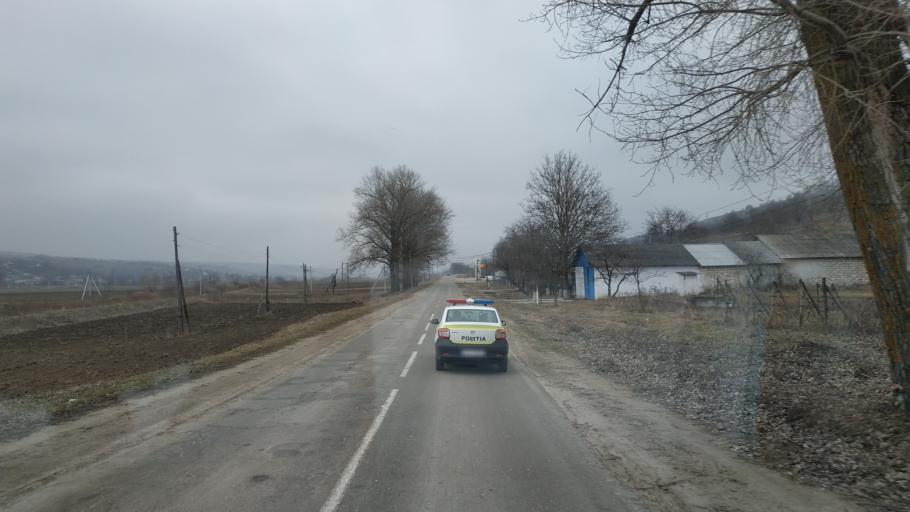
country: MD
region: Hincesti
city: Hincesti
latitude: 46.9737
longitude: 28.4722
